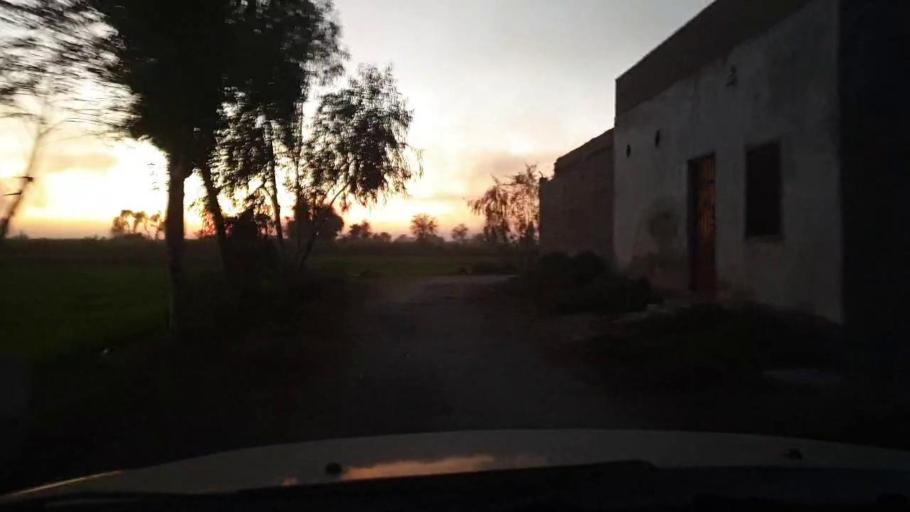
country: PK
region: Sindh
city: Ghotki
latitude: 27.9849
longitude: 69.2821
